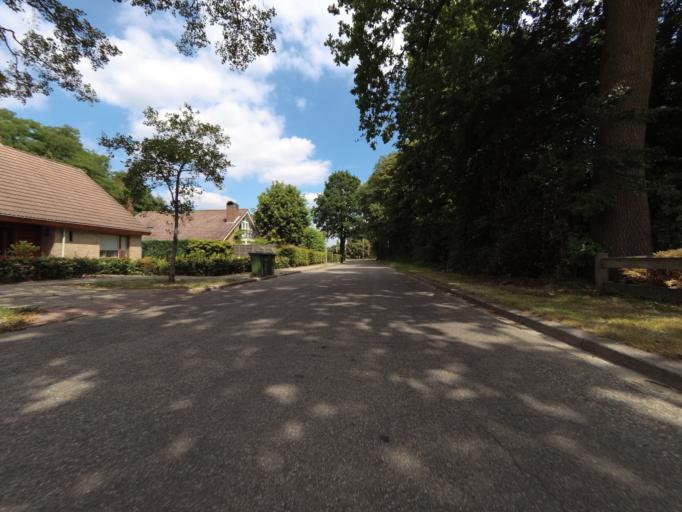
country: NL
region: Overijssel
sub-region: Gemeente Twenterand
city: Den Ham
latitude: 52.3515
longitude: 6.4689
